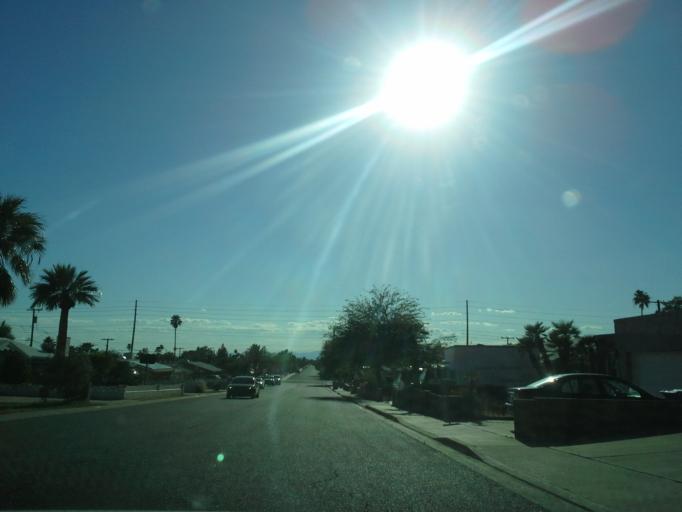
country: US
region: Arizona
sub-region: Maricopa County
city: Paradise Valley
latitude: 33.5642
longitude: -112.0548
